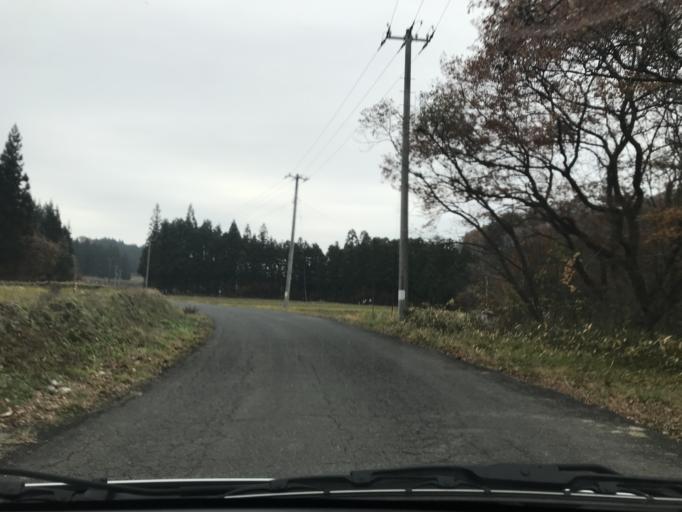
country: JP
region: Iwate
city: Ichinoseki
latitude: 39.0126
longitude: 141.0719
